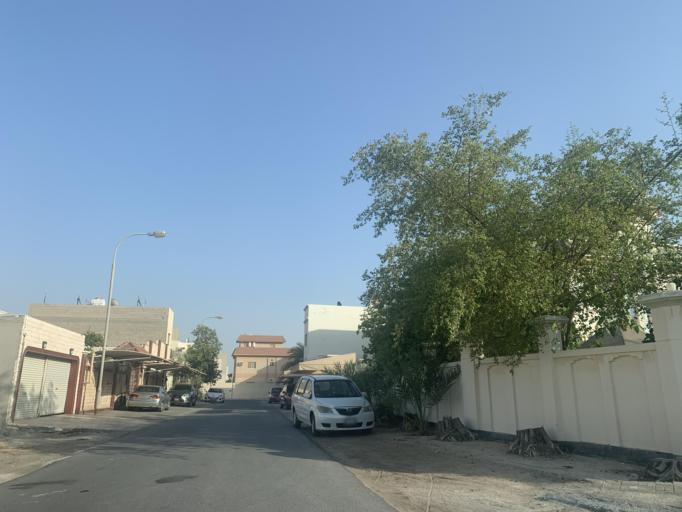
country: BH
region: Manama
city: Jidd Hafs
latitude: 26.2107
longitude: 50.5326
